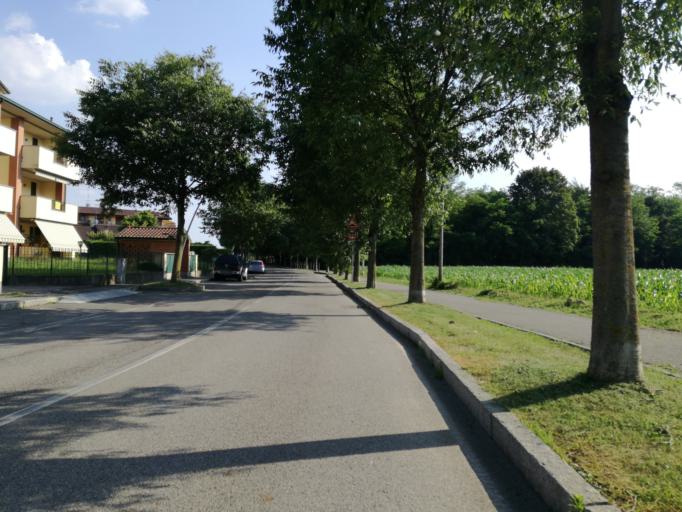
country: IT
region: Lombardy
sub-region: Provincia di Bergamo
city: Calusco d'Adda
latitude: 45.6913
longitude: 9.4581
